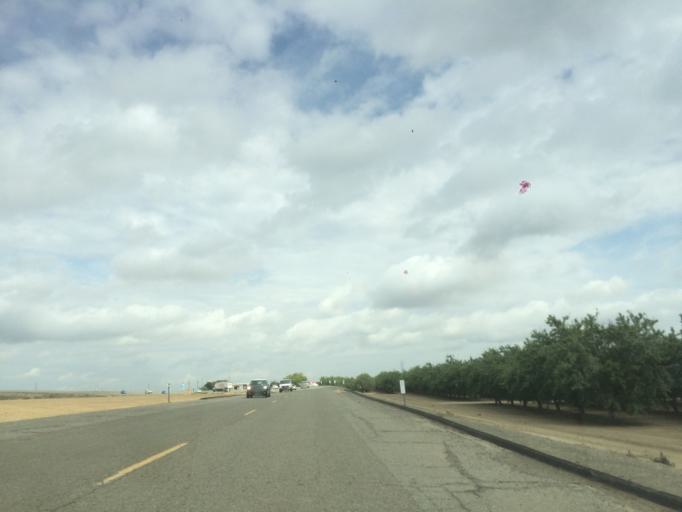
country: US
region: California
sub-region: Fresno County
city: Coalinga
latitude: 36.3663
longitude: -120.3309
